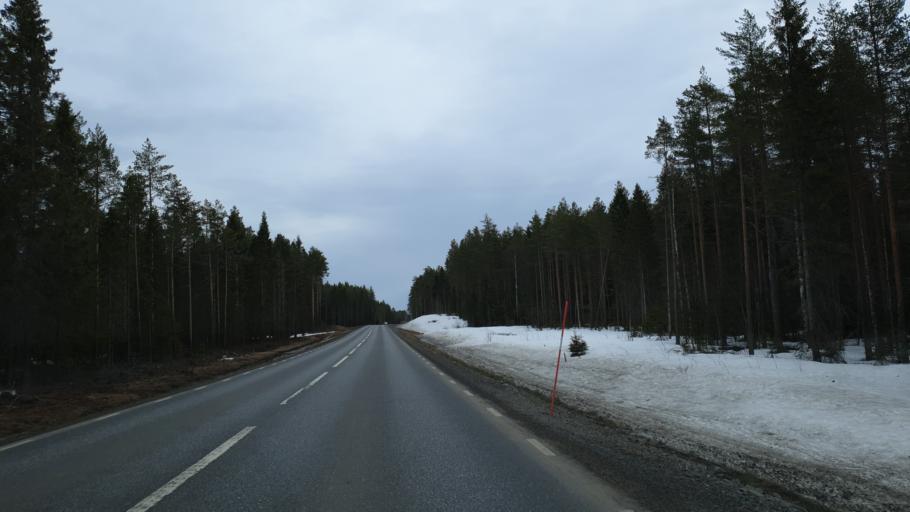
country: SE
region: Vaesterbotten
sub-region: Robertsfors Kommun
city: Robertsfors
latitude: 64.2134
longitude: 20.8885
